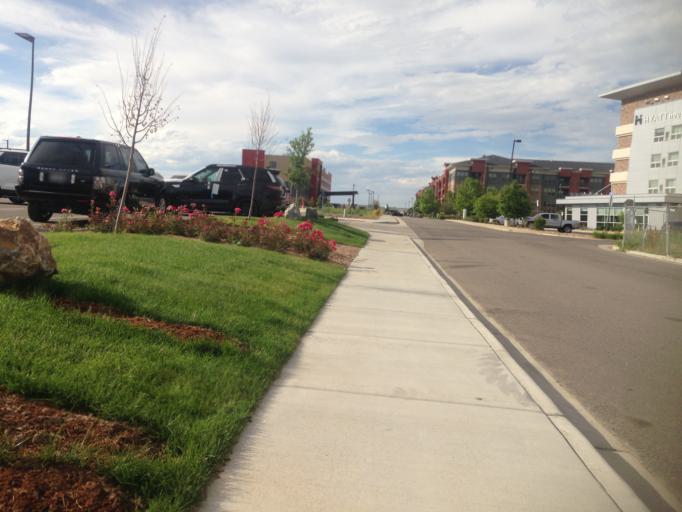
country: US
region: Colorado
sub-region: Boulder County
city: Louisville
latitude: 39.9395
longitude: -105.1255
